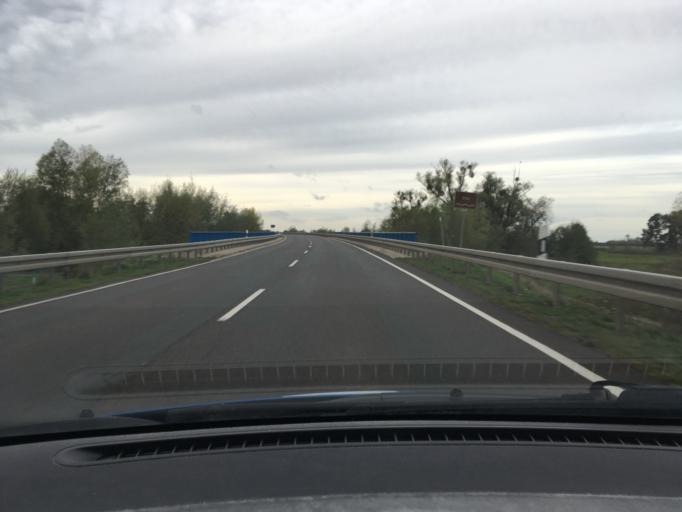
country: DE
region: Saxony-Anhalt
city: Gommern
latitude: 52.0750
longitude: 11.8761
